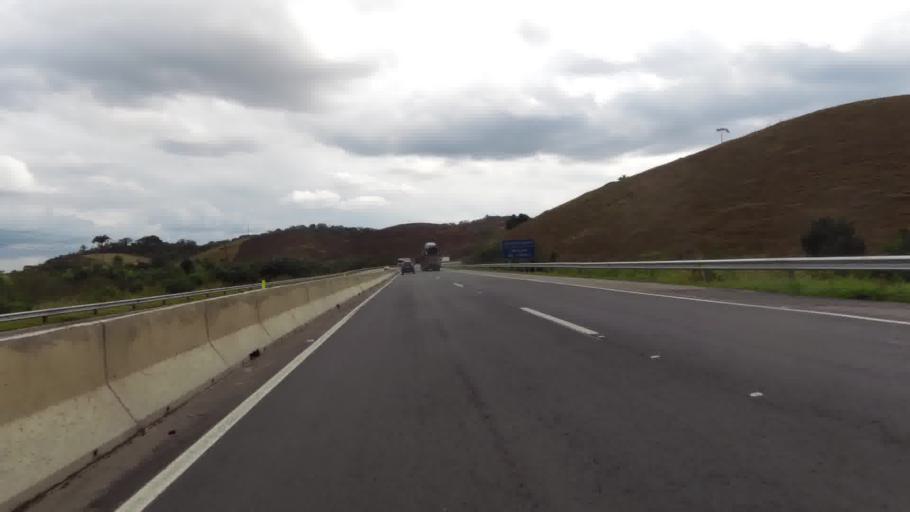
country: BR
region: Rio de Janeiro
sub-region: Casimiro De Abreu
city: Casimiro de Abreu
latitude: -22.4712
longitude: -42.0787
